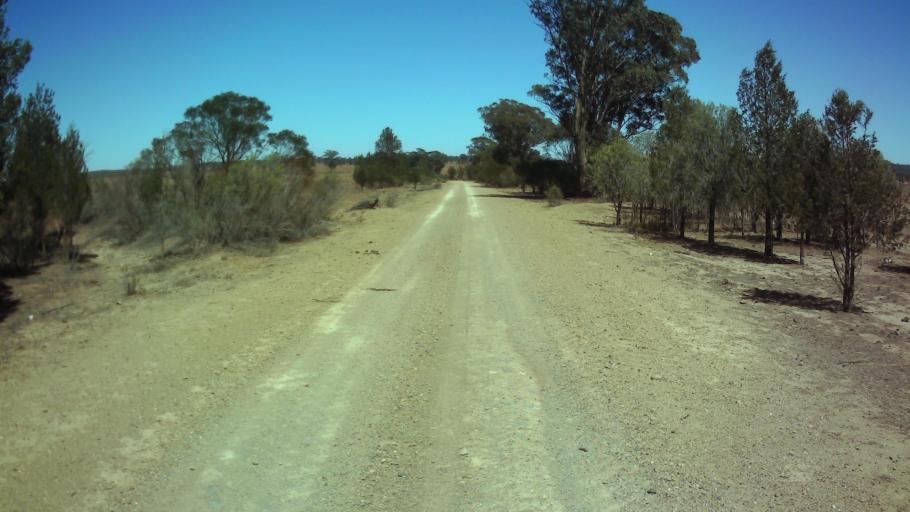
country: AU
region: New South Wales
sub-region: Forbes
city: Forbes
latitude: -33.6946
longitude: 147.8310
